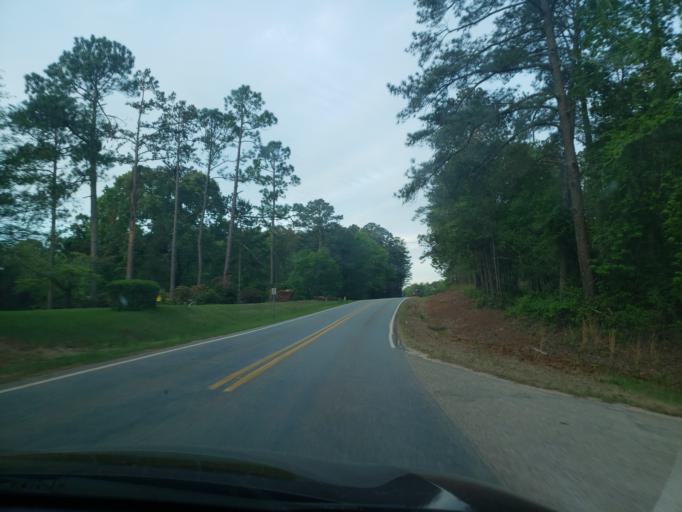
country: US
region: Alabama
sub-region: Tallapoosa County
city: Dadeville
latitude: 32.7044
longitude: -85.8380
